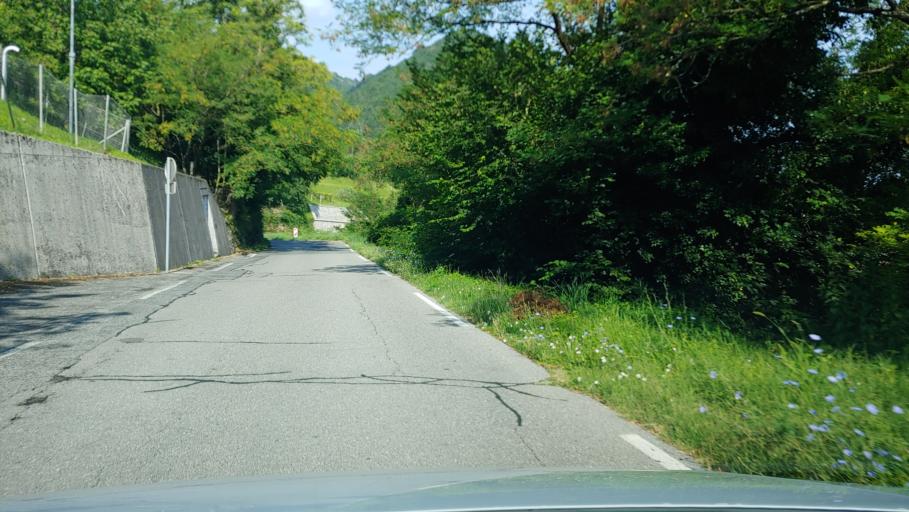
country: SI
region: Komen
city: Komen
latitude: 45.8528
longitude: 13.7916
